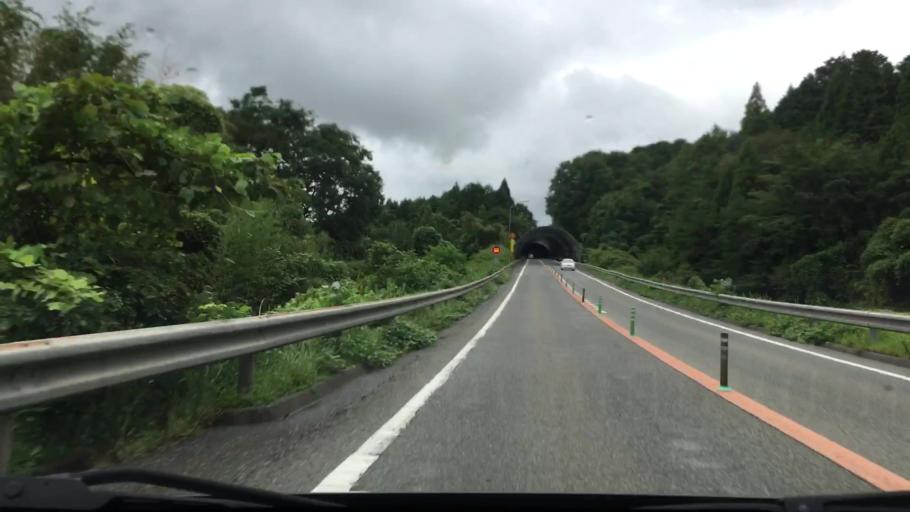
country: JP
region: Hyogo
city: Nishiwaki
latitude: 35.0812
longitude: 134.7734
